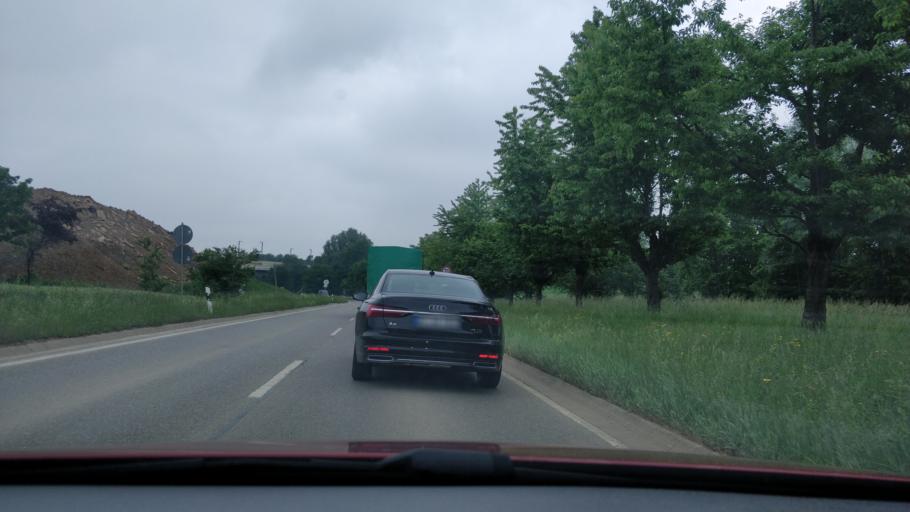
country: DE
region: Baden-Wuerttemberg
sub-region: Regierungsbezirk Stuttgart
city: Denkendorf
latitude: 48.6898
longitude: 9.3082
